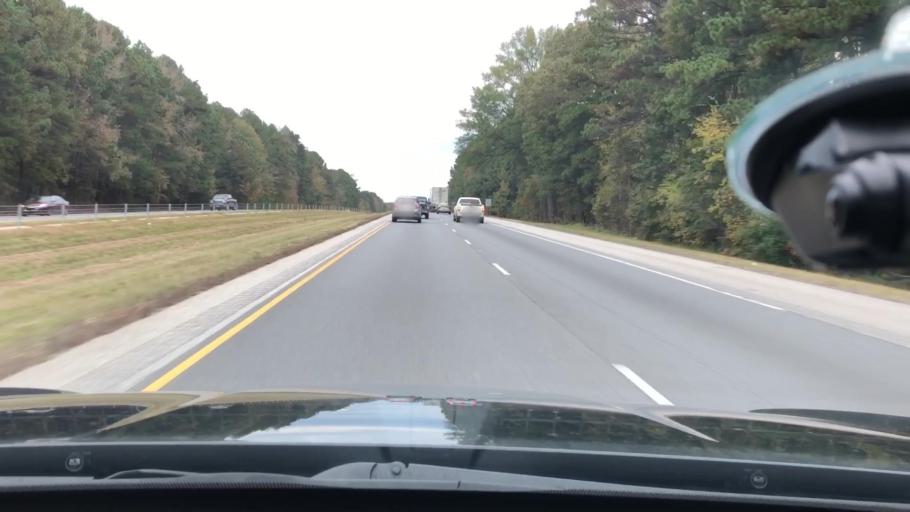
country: US
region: Arkansas
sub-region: Clark County
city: Arkadelphia
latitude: 34.1266
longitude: -93.0885
